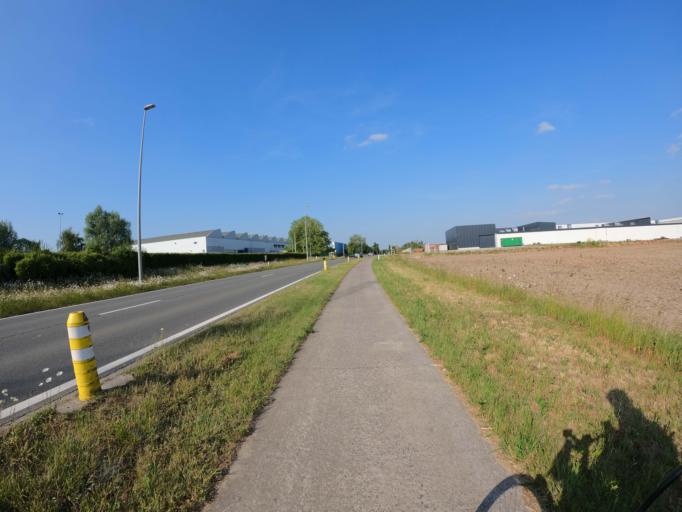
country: BE
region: Flanders
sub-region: Provincie West-Vlaanderen
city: Ingelmunster
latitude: 50.9338
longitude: 3.2653
